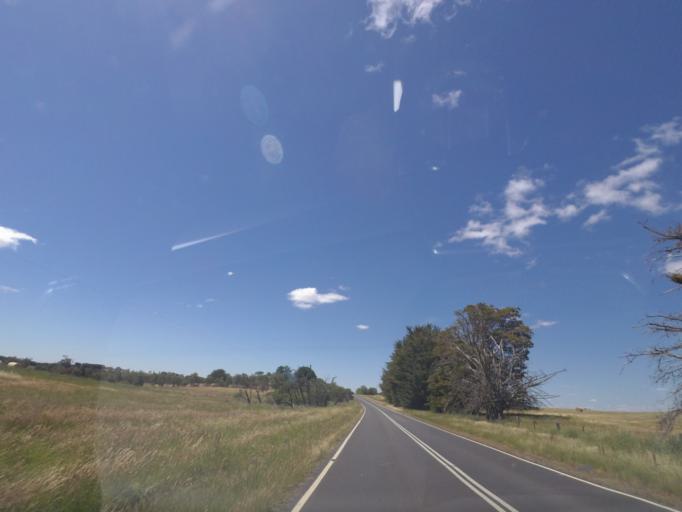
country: AU
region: Victoria
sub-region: Mount Alexander
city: Castlemaine
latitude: -37.2430
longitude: 144.3250
